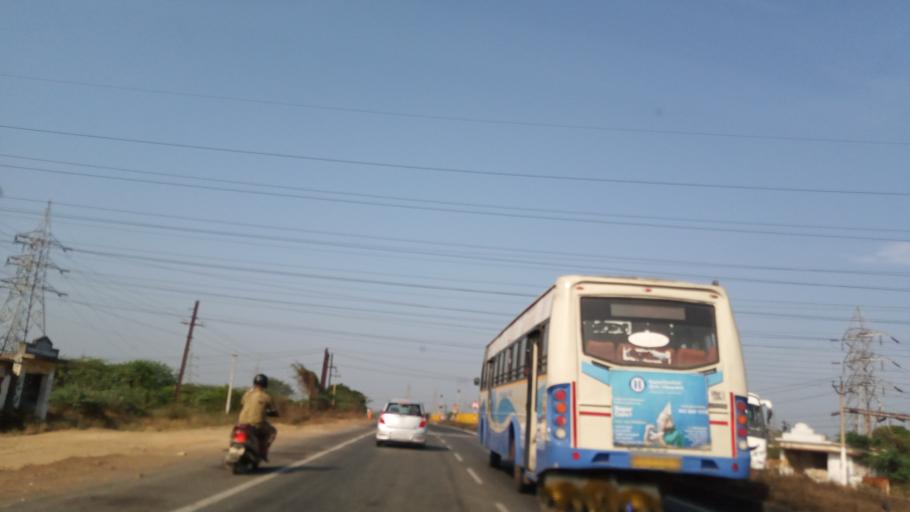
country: IN
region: Tamil Nadu
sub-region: Kancheepuram
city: Sriperumbudur
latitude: 12.9849
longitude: 79.9752
